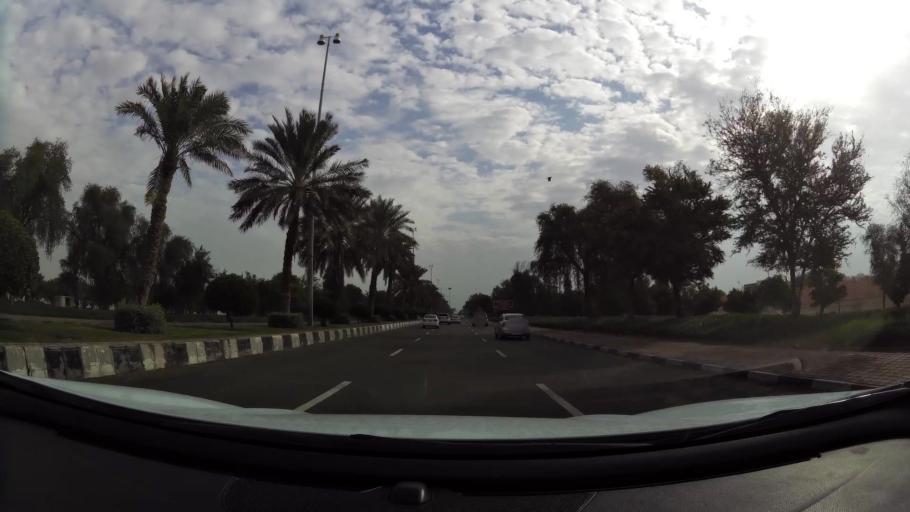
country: AE
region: Abu Dhabi
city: Al Ain
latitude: 24.1923
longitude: 55.6498
